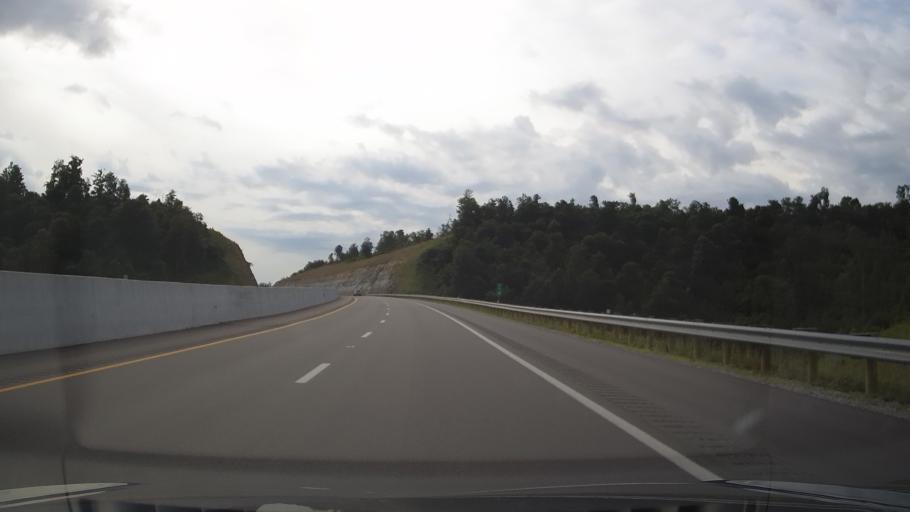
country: US
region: Ohio
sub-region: Scioto County
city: Lucasville
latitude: 38.8949
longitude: -82.9564
